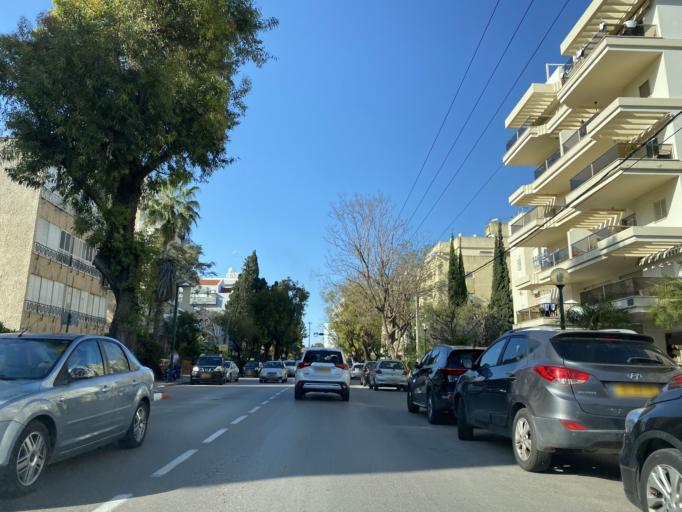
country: IL
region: Central District
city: Kfar Saba
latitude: 32.1753
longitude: 34.9145
